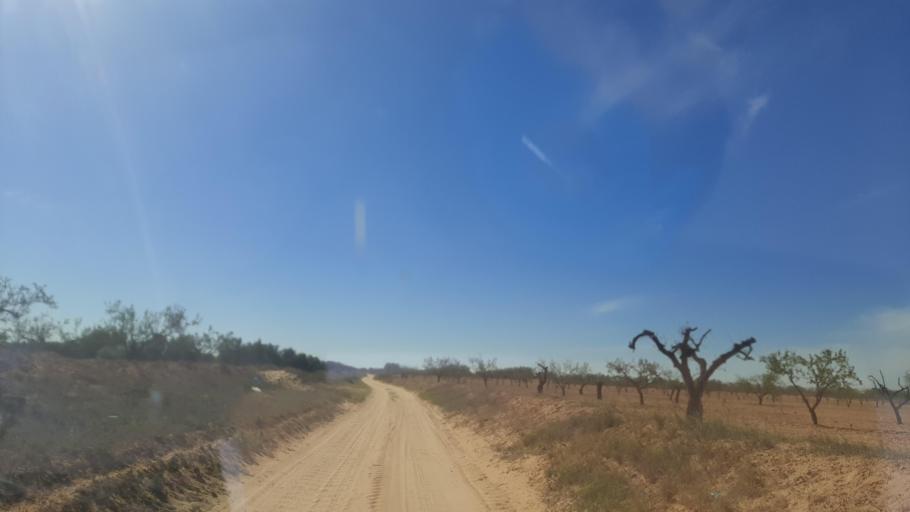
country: TN
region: Safaqis
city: Sfax
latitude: 34.8263
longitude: 10.5544
